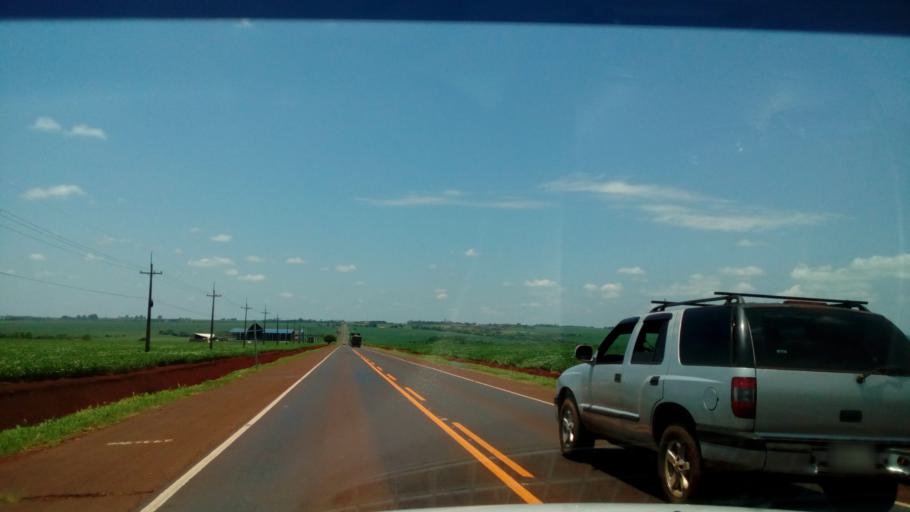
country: PY
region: Alto Parana
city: Naranjal
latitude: -25.8907
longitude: -55.1227
